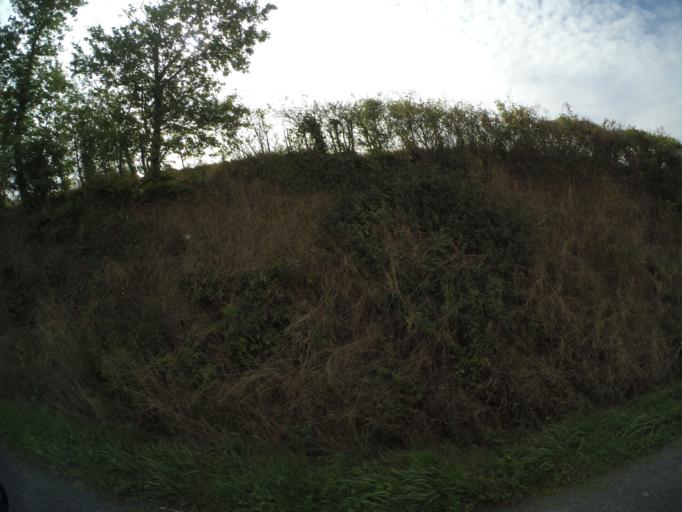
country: FR
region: Pays de la Loire
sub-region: Departement de Maine-et-Loire
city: Martigne-Briand
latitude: 47.2051
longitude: -0.4537
